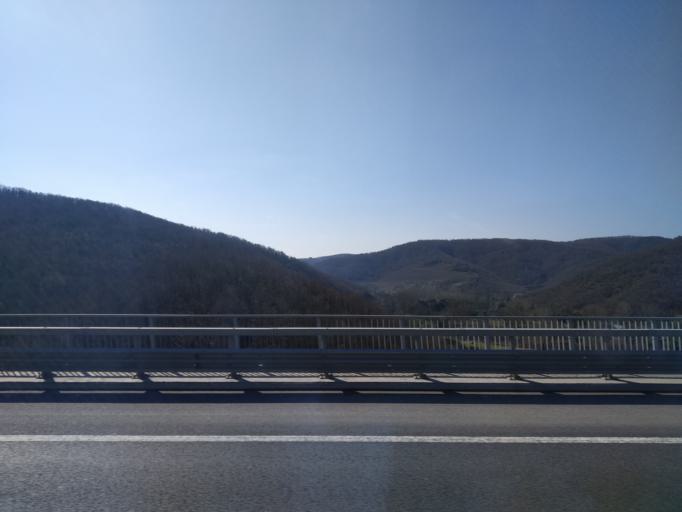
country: TR
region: Istanbul
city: Mahmut Sevket Pasa
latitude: 41.1521
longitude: 29.2691
